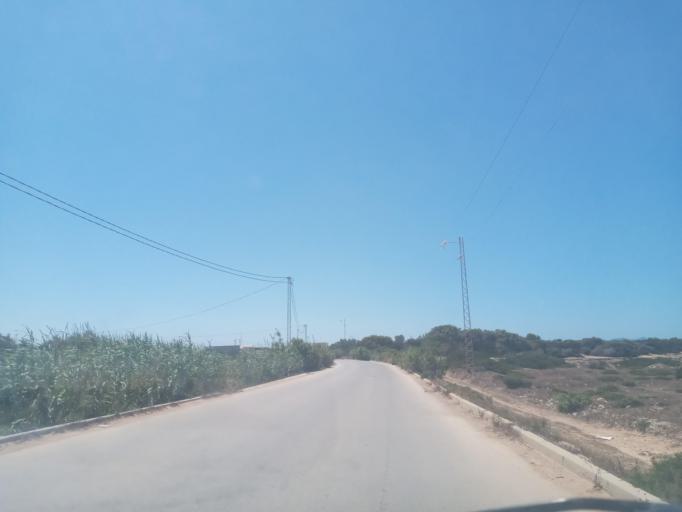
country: TN
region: Nabul
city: El Haouaria
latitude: 37.0497
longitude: 10.9685
